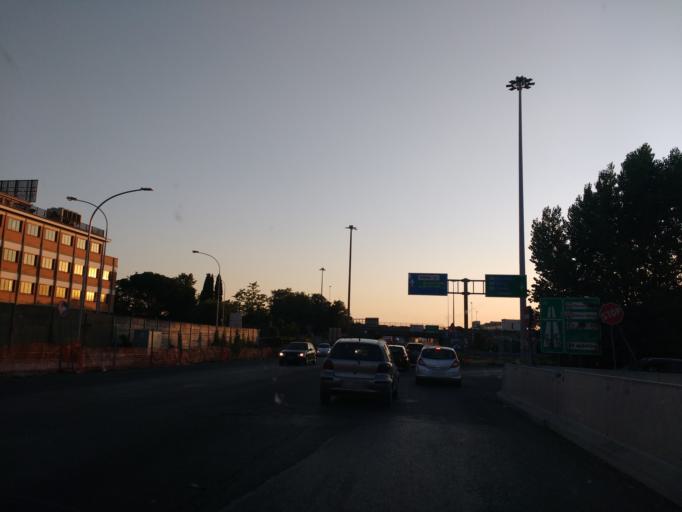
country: IT
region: Latium
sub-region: Citta metropolitana di Roma Capitale
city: Colle Verde
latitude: 41.9337
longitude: 12.6031
